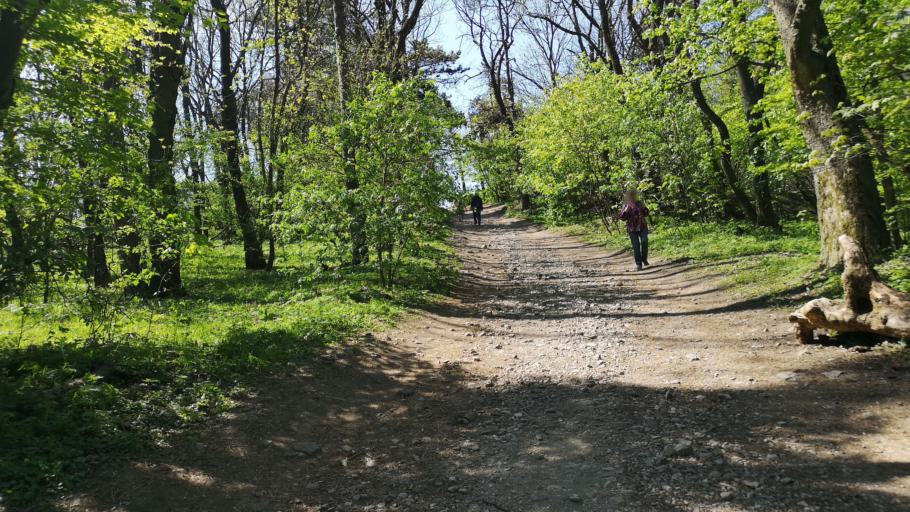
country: SK
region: Nitriansky
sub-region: Okres Nitra
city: Nitra
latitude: 48.3440
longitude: 18.1055
